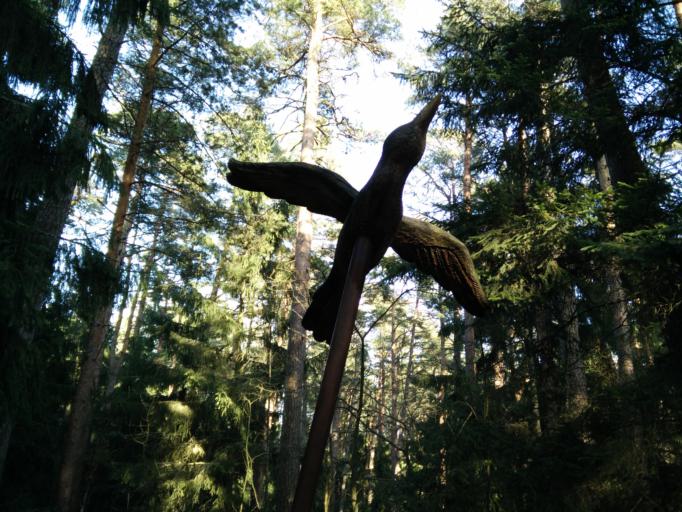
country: LT
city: Neringa
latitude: 55.5365
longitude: 21.1108
